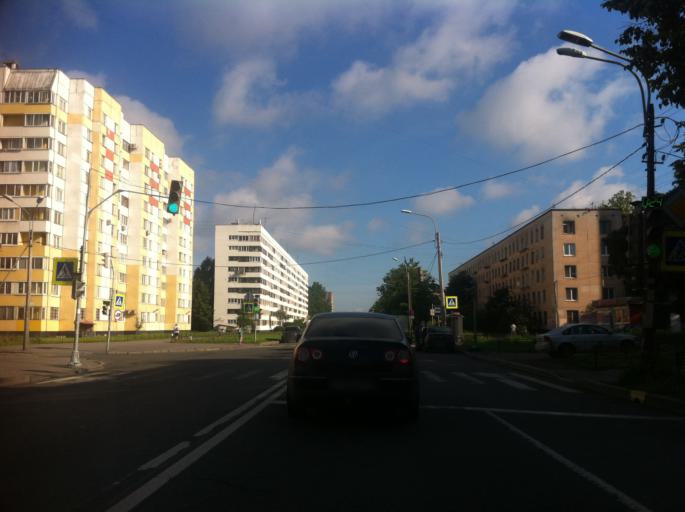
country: RU
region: St.-Petersburg
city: Dachnoye
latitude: 59.8287
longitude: 30.2216
